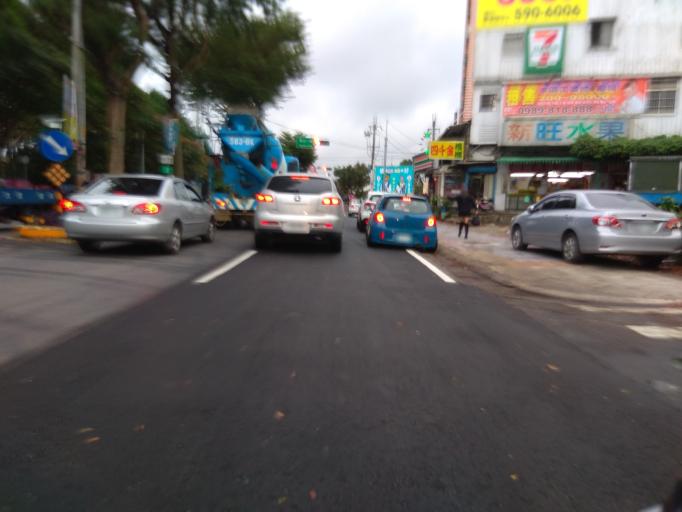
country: TW
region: Taiwan
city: Daxi
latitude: 24.9232
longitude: 121.1774
